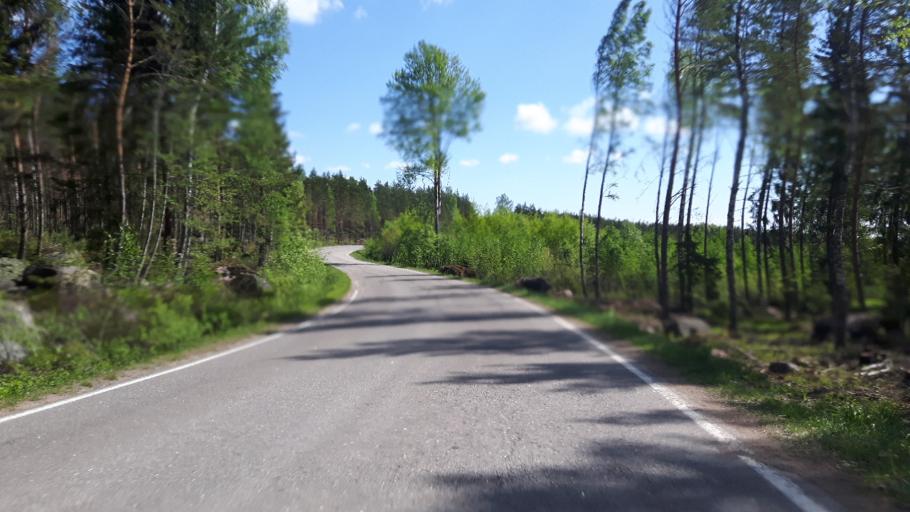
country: FI
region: Kymenlaakso
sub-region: Kotka-Hamina
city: Hamina
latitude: 60.5138
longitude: 27.4246
